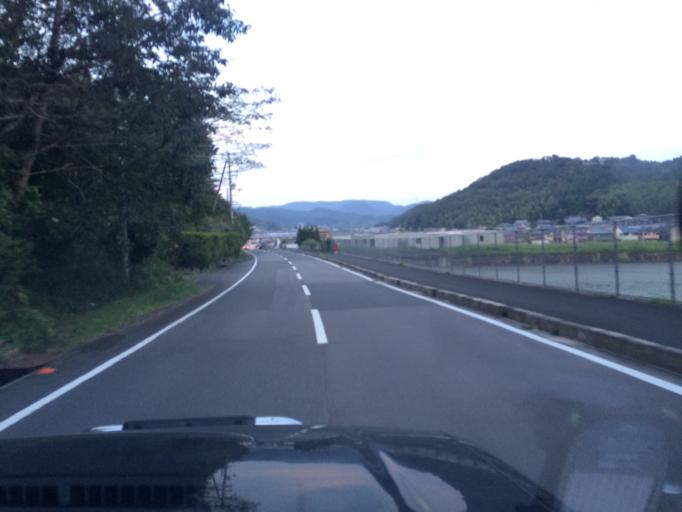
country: JP
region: Kyoto
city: Kameoka
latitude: 35.0918
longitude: 135.4759
